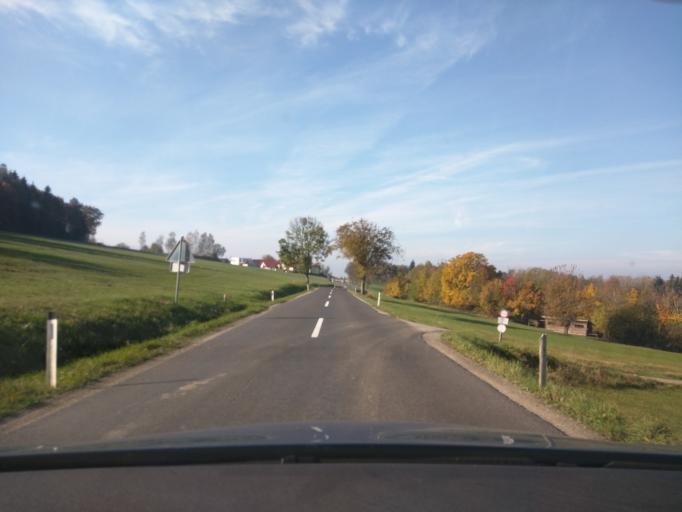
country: DE
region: Bavaria
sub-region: Lower Bavaria
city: Thyrnau
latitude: 48.5633
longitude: 13.5294
